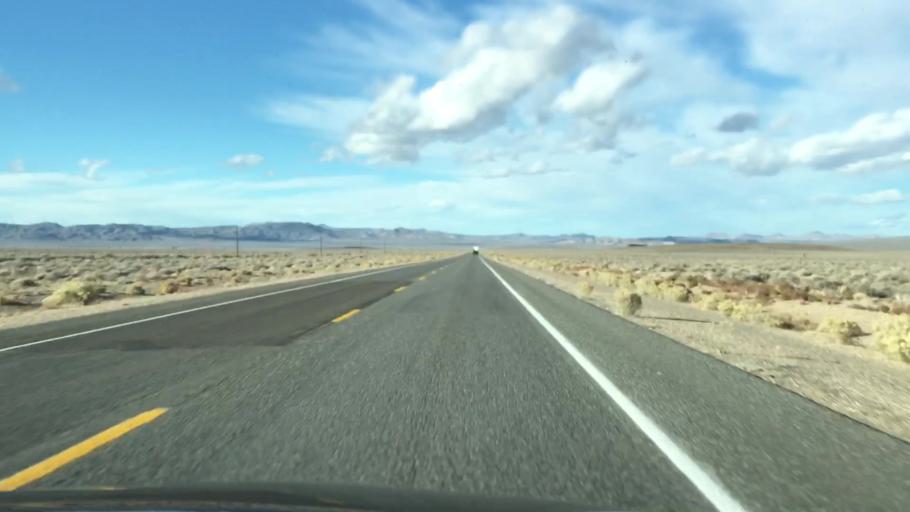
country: US
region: Nevada
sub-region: Esmeralda County
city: Goldfield
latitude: 37.4055
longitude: -117.1507
